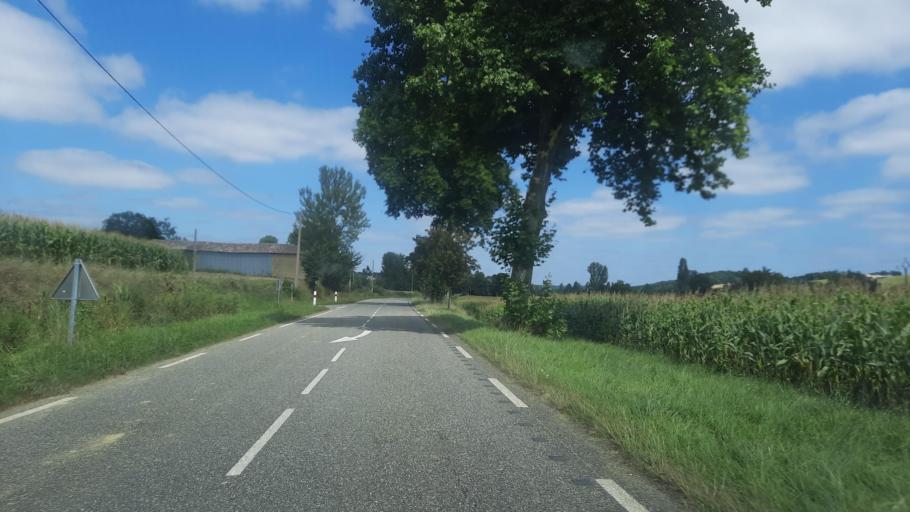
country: FR
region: Midi-Pyrenees
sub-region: Departement de la Haute-Garonne
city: Boulogne-sur-Gesse
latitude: 43.3818
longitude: 0.7666
